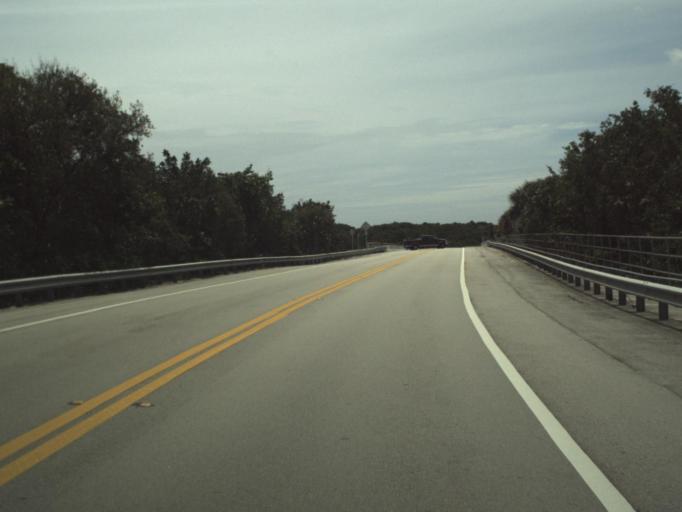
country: US
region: Florida
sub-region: Palm Beach County
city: Lake Park
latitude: 26.8200
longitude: -80.0411
